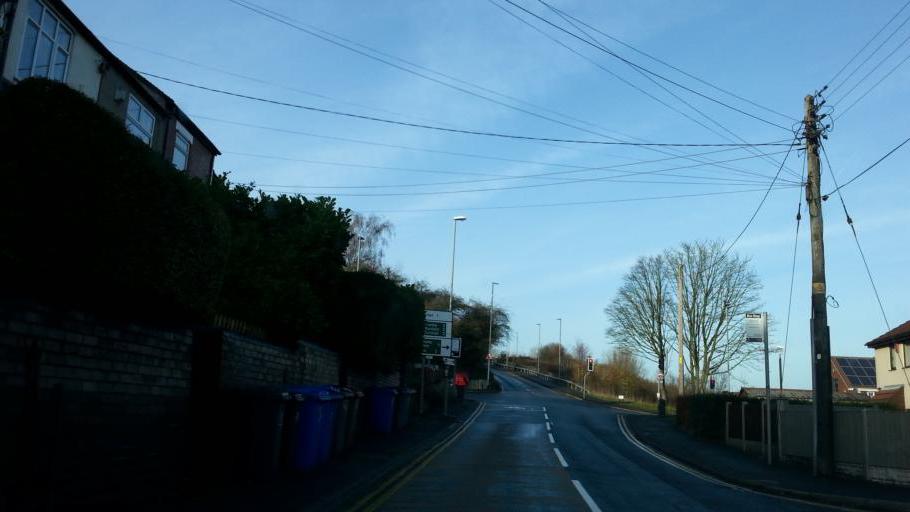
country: GB
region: England
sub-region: Stoke-on-Trent
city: Stoke-on-Trent
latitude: 53.0512
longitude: -2.1515
